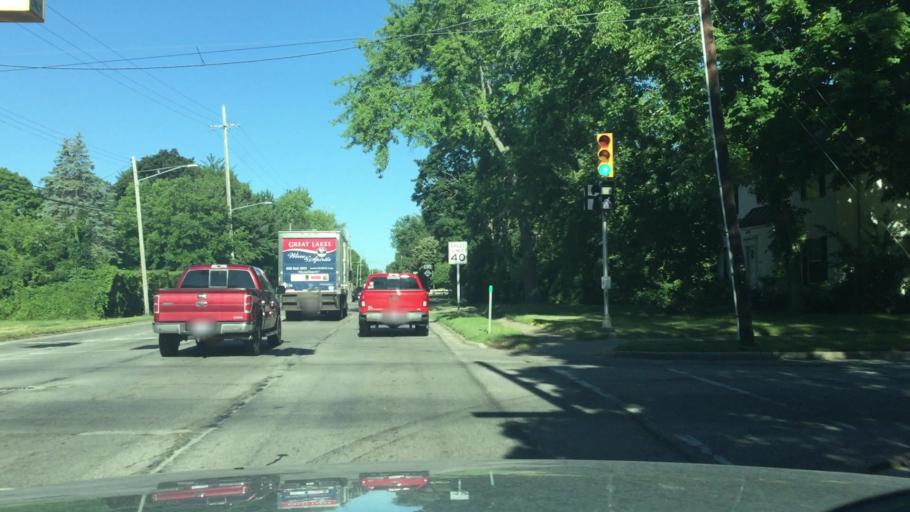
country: US
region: Michigan
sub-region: Saginaw County
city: Saginaw
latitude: 43.4152
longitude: -83.9913
